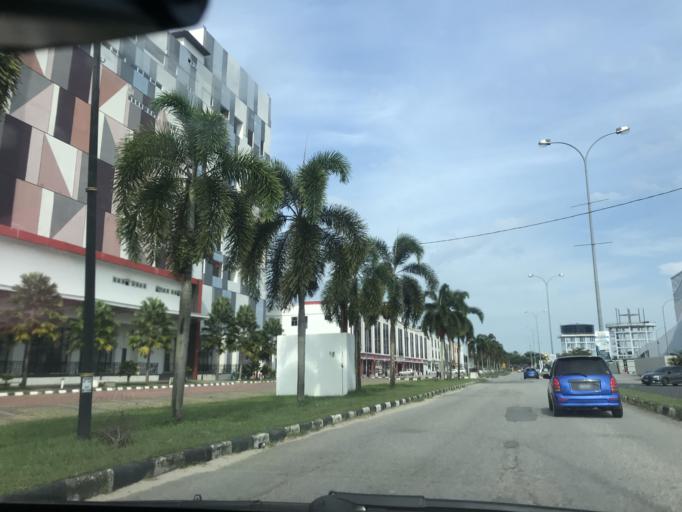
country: MY
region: Kelantan
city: Kota Bharu
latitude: 6.1126
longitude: 102.2305
